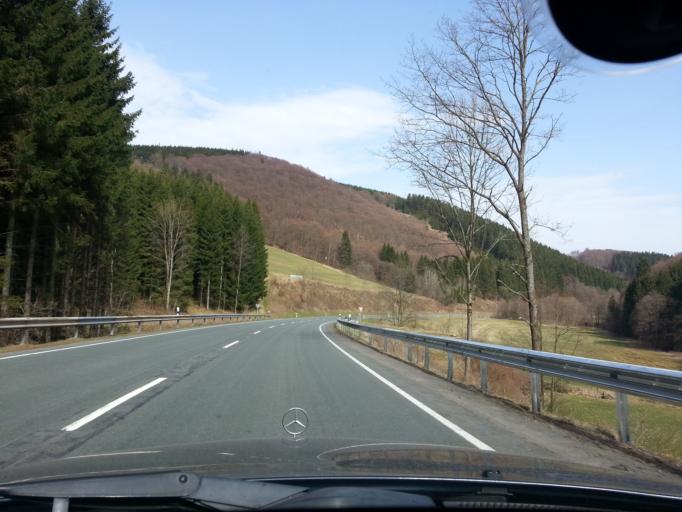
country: DE
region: North Rhine-Westphalia
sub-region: Regierungsbezirk Arnsberg
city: Bad Fredeburg
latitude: 51.2274
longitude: 8.3531
